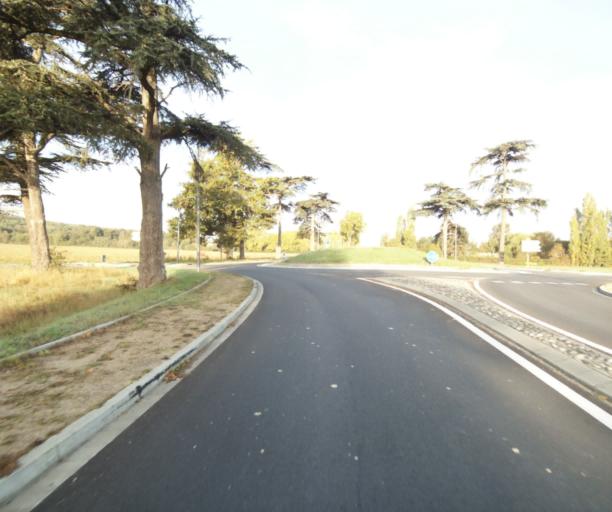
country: FR
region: Midi-Pyrenees
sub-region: Departement du Tarn-et-Garonne
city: Saint-Nauphary
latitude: 43.9440
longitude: 1.4639
